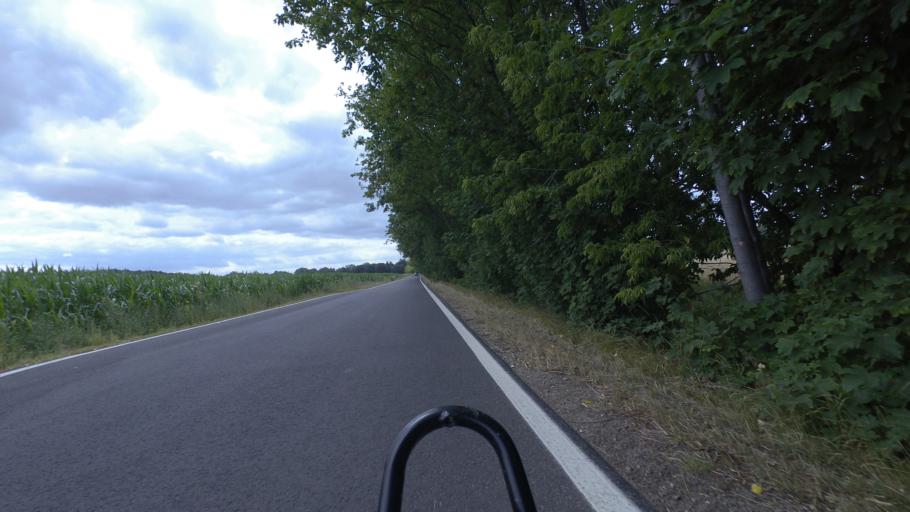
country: DE
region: Brandenburg
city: Ludwigsfelde
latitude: 52.2545
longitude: 13.3004
